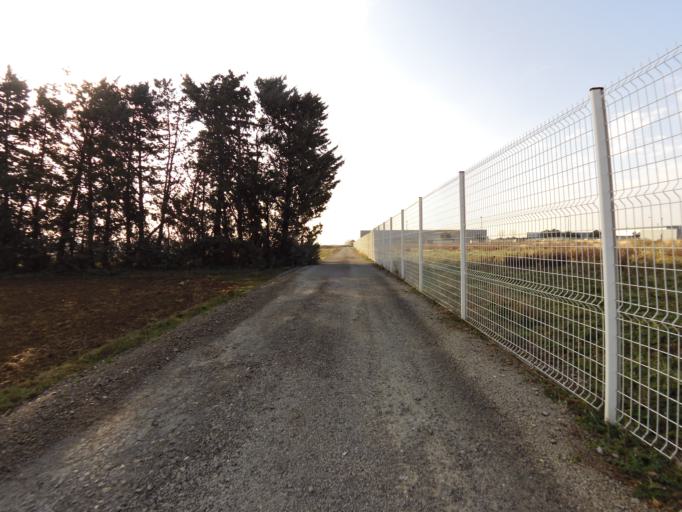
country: FR
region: Languedoc-Roussillon
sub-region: Departement du Gard
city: Aigues-Vives
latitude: 43.7234
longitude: 4.1904
